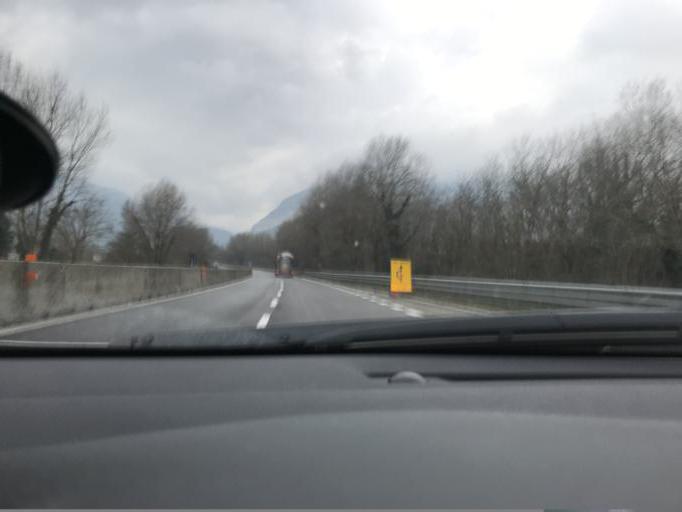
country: IT
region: The Marches
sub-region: Provincia di Ancona
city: Serra San Quirico
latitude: 43.4499
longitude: 13.0385
